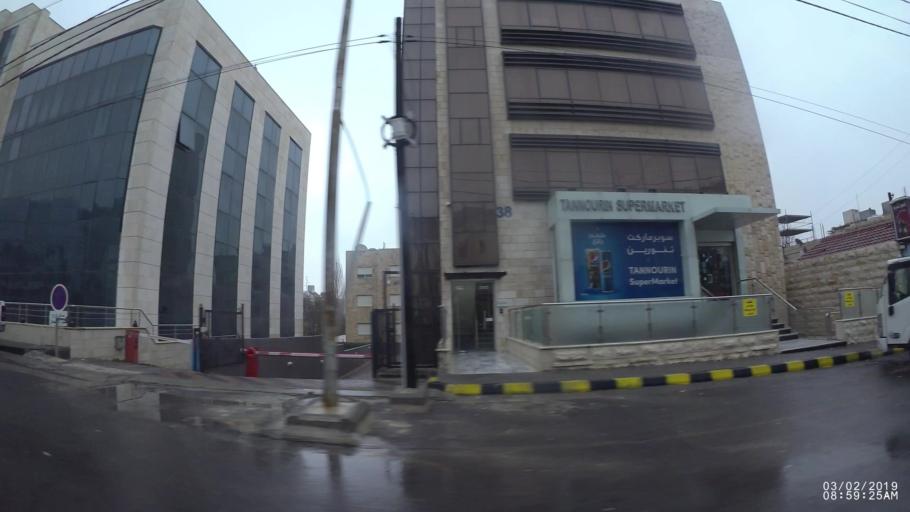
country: JO
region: Amman
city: Al Jubayhah
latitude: 31.9679
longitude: 35.8774
